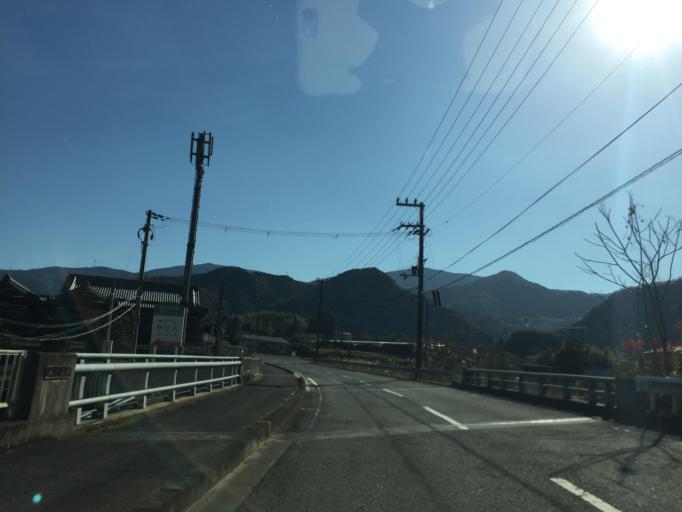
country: JP
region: Wakayama
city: Iwade
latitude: 34.1486
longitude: 135.3463
